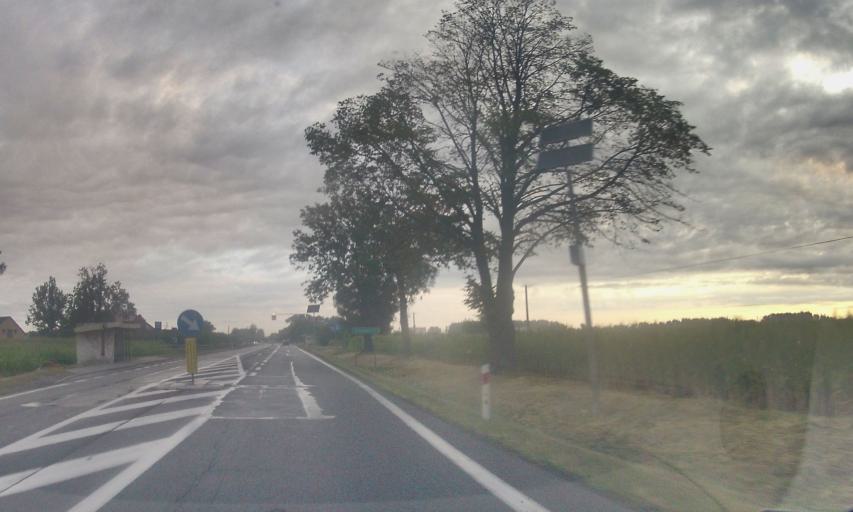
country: PL
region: Masovian Voivodeship
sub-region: Powiat plonski
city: Plonsk
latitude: 52.6724
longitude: 20.3719
